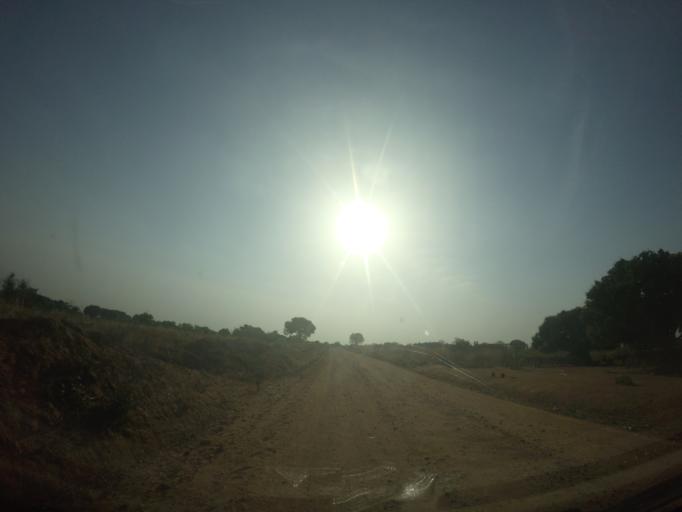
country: UG
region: Northern Region
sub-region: Arua District
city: Arua
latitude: 3.1100
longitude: 31.1208
